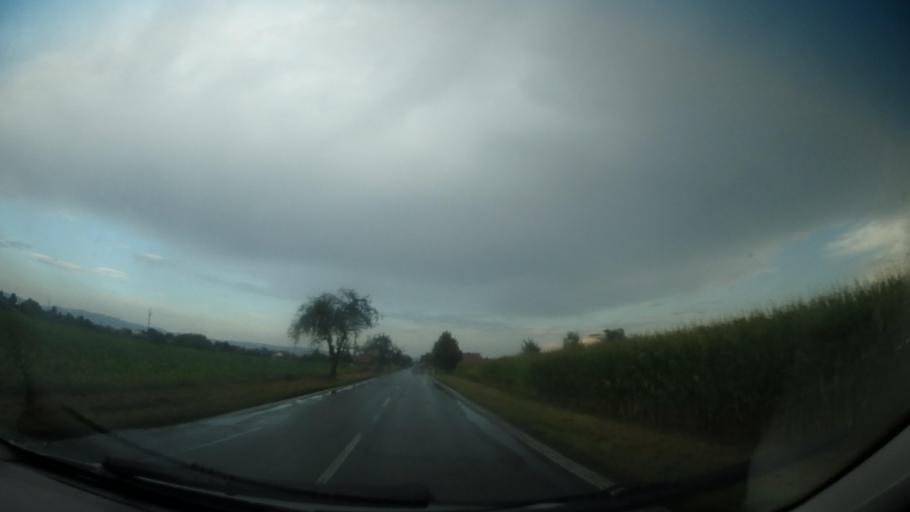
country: CZ
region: Olomoucky
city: Ujezd
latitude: 49.7159
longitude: 17.1513
